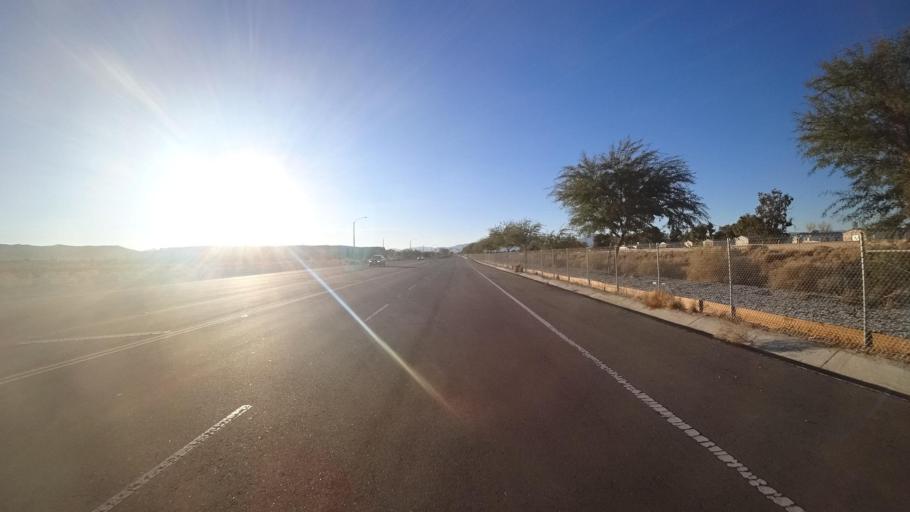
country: US
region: California
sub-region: Kern County
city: Ridgecrest
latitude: 35.6080
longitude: -117.6640
